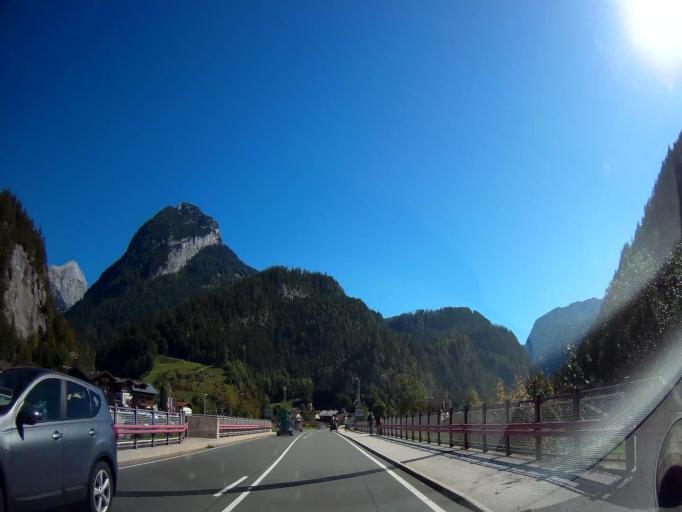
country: AT
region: Salzburg
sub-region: Politischer Bezirk Zell am See
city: Sankt Martin bei Lofer
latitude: 47.5227
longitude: 12.7505
